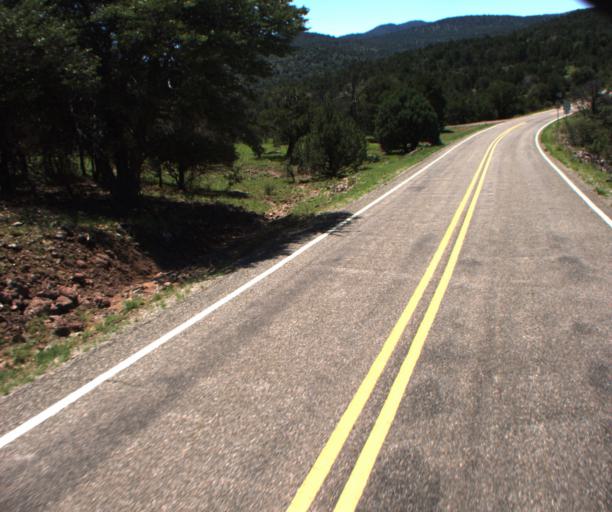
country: US
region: Arizona
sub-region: Greenlee County
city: Morenci
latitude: 33.2725
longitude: -109.3580
